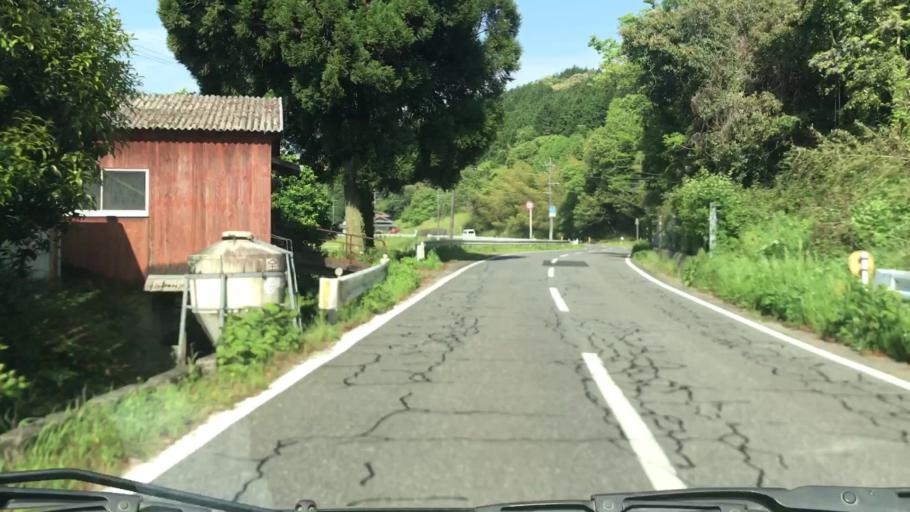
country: JP
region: Saga Prefecture
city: Takeocho-takeo
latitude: 33.2150
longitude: 129.9891
